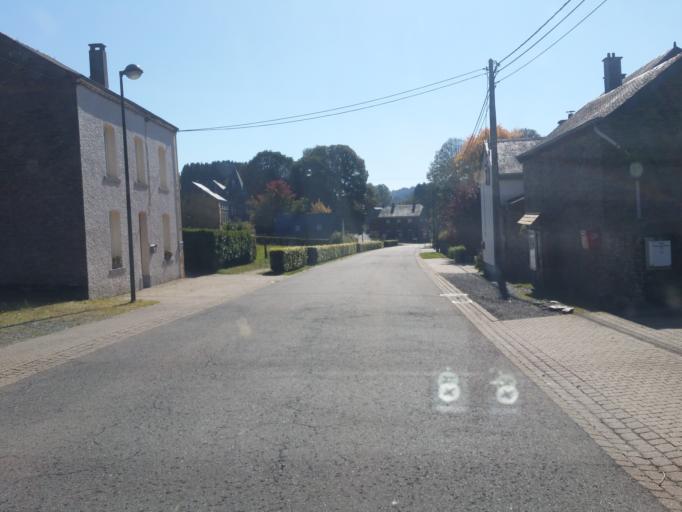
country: BE
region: Wallonia
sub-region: Province du Luxembourg
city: Herbeumont
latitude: 49.7791
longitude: 5.2391
